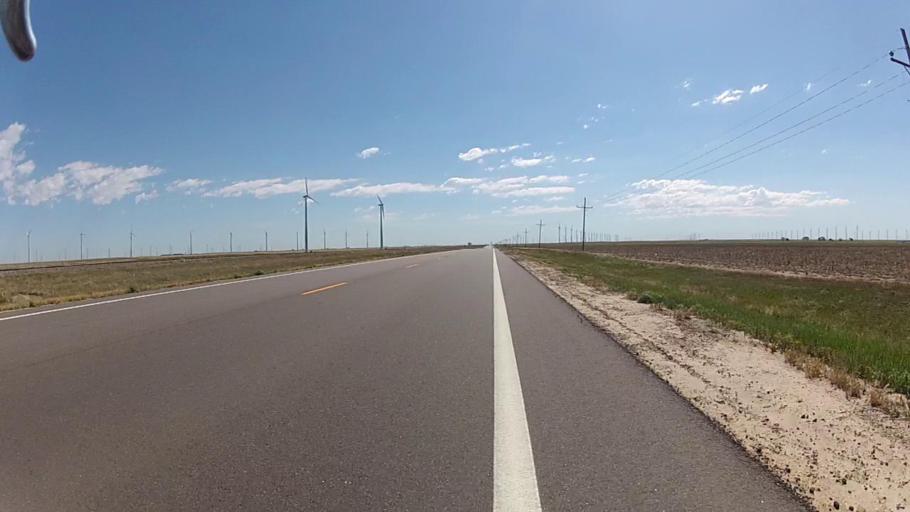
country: US
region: Kansas
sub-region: Gray County
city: Cimarron
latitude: 37.6100
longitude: -100.4046
